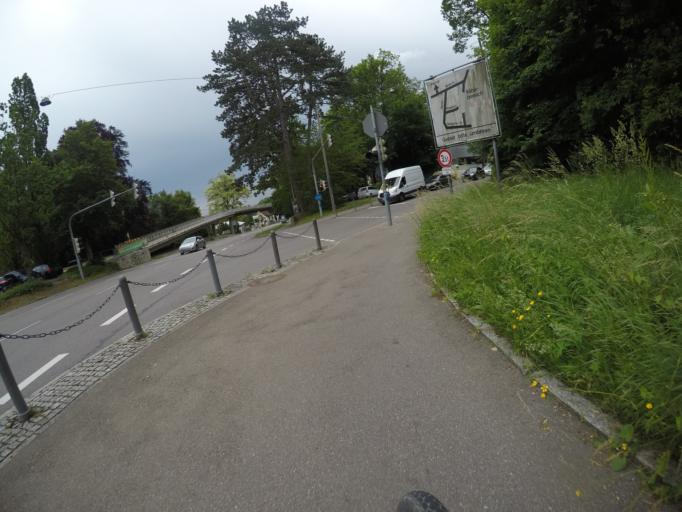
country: DE
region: Baden-Wuerttemberg
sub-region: Tuebingen Region
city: Ulm
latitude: 48.4123
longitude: 9.9921
